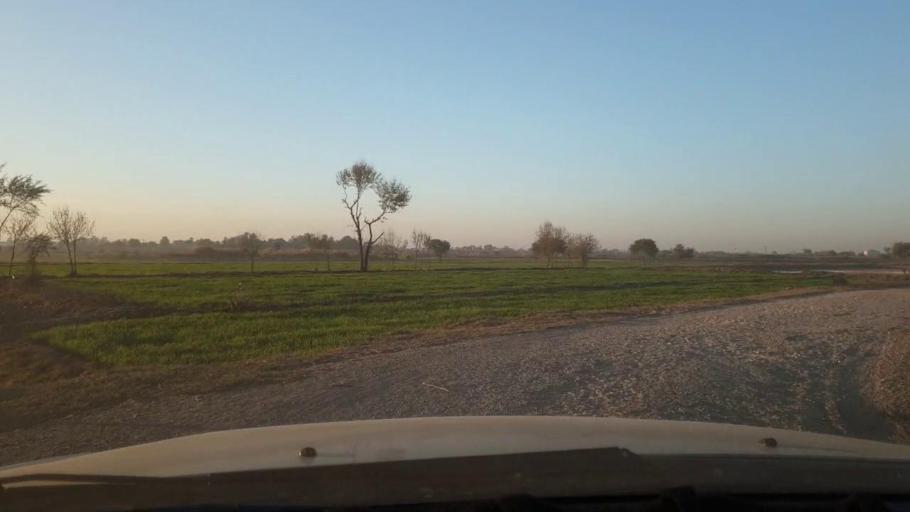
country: PK
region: Sindh
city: Pano Aqil
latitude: 27.9133
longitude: 69.1939
